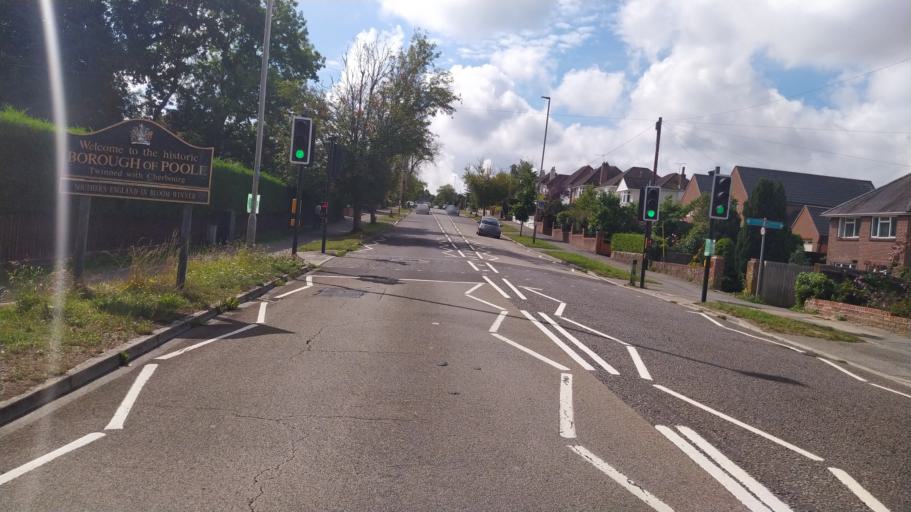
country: GB
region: England
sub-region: Dorset
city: Wimborne Minster
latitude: 50.7910
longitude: -1.9774
